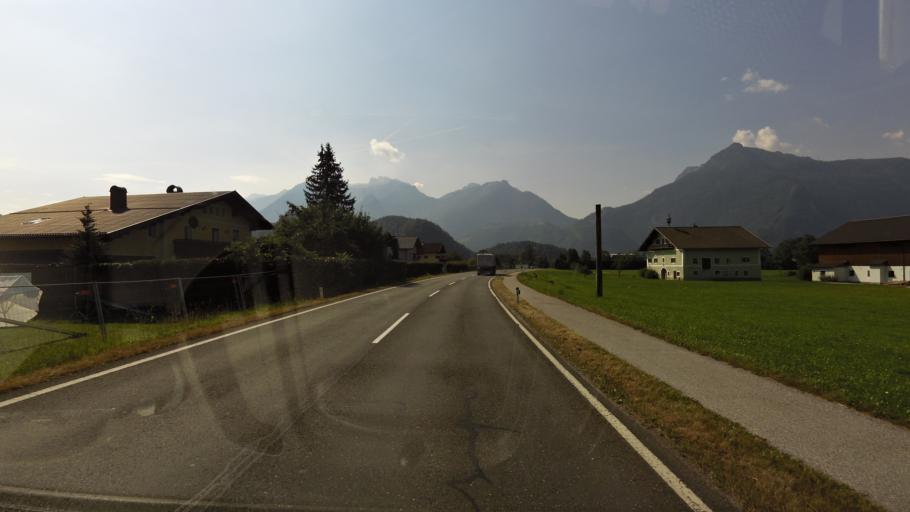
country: AT
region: Salzburg
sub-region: Politischer Bezirk Hallein
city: Golling an der Salzach
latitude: 47.6125
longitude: 13.1670
